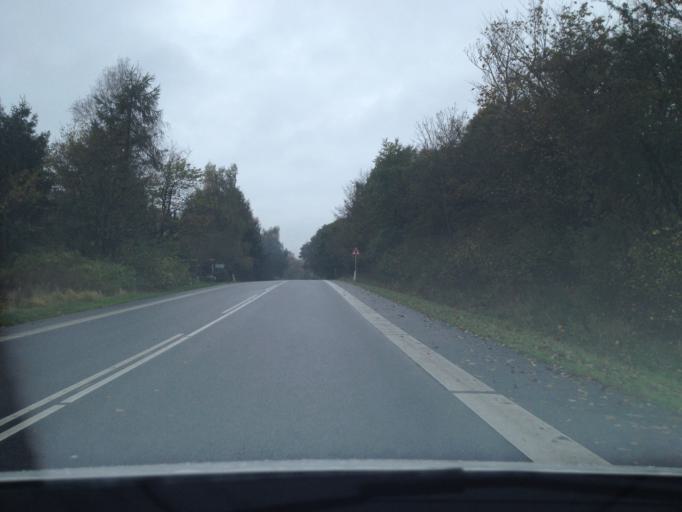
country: DK
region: Capital Region
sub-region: Fredensborg Kommune
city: Kokkedal
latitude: 55.9201
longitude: 12.4511
